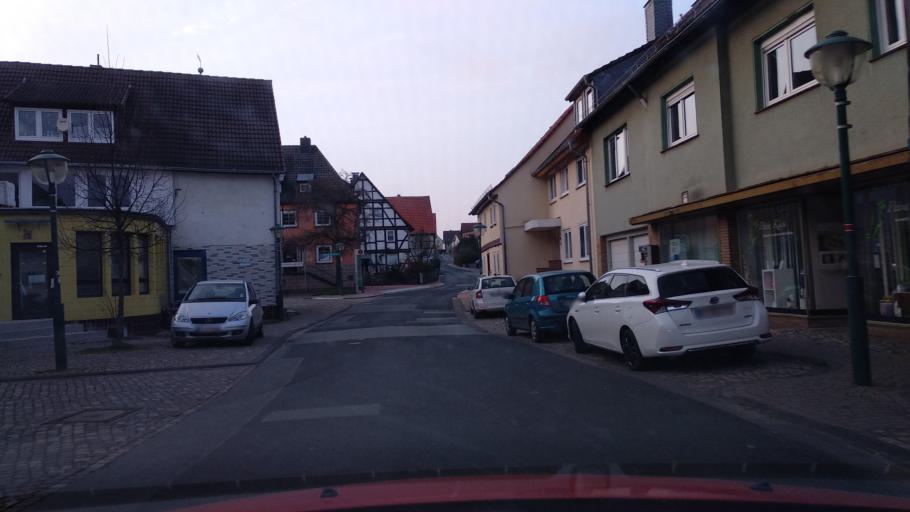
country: DE
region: Hesse
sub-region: Regierungsbezirk Kassel
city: Calden
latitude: 51.3667
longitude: 9.3930
